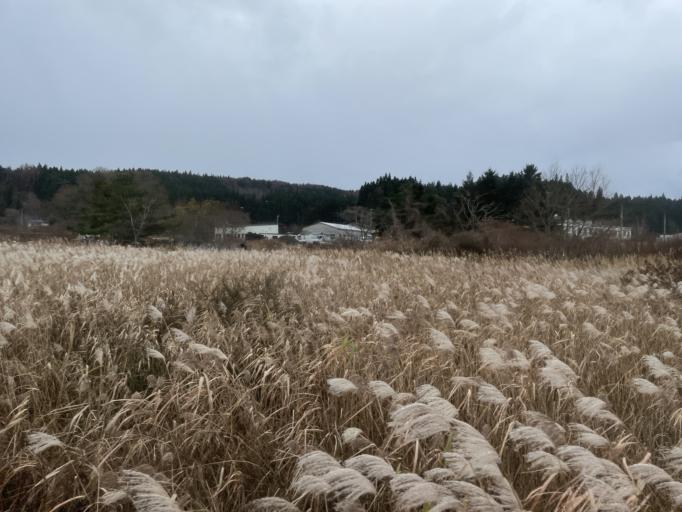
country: JP
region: Aomori
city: Goshogawara
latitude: 41.1765
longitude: 140.4945
